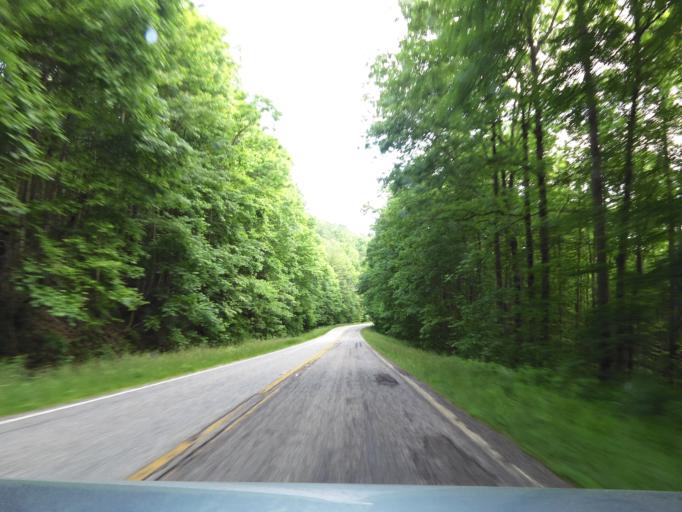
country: US
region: Georgia
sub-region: Towns County
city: Hiawassee
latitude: 34.8456
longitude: -83.7986
